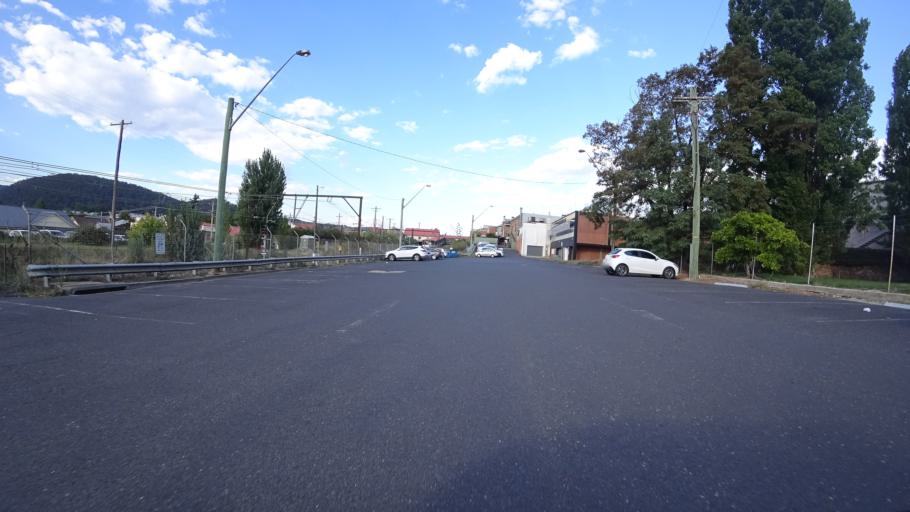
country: AU
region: New South Wales
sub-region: Lithgow
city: Lithgow
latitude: -33.4813
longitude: 150.1549
